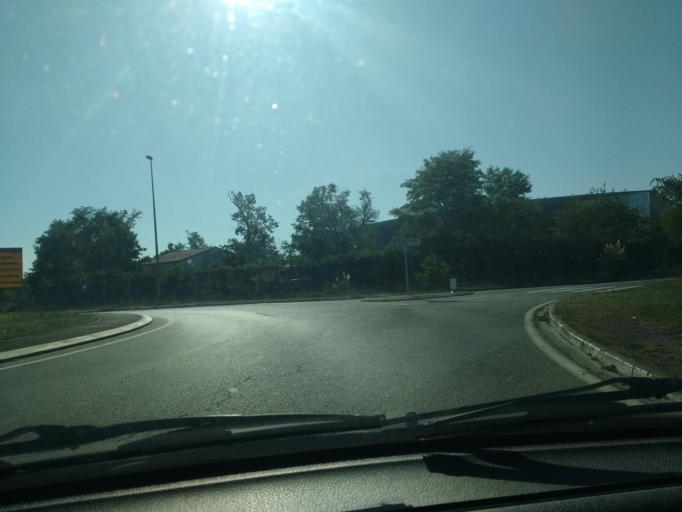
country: FR
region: Aquitaine
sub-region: Departement de la Gironde
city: Le Haillan
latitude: 44.8479
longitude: -0.7082
